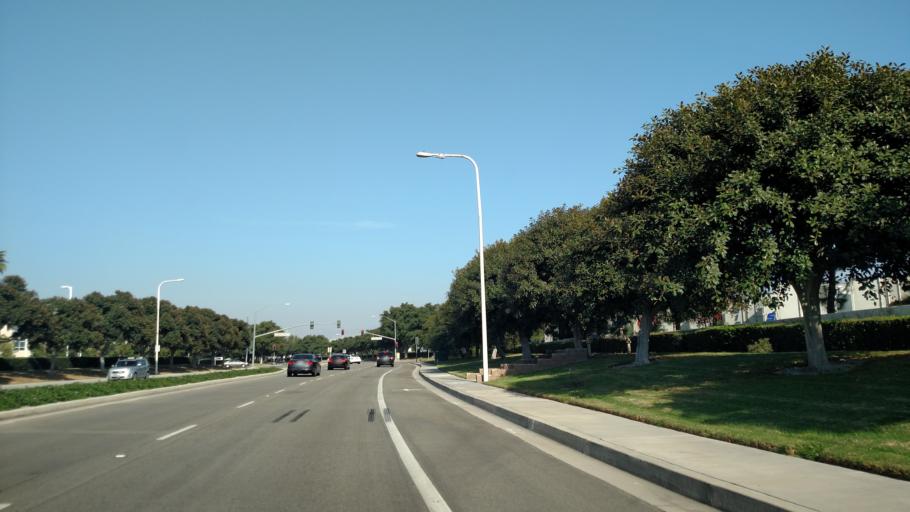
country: US
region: California
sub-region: Orange County
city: Irvine
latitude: 33.6637
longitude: -117.7643
